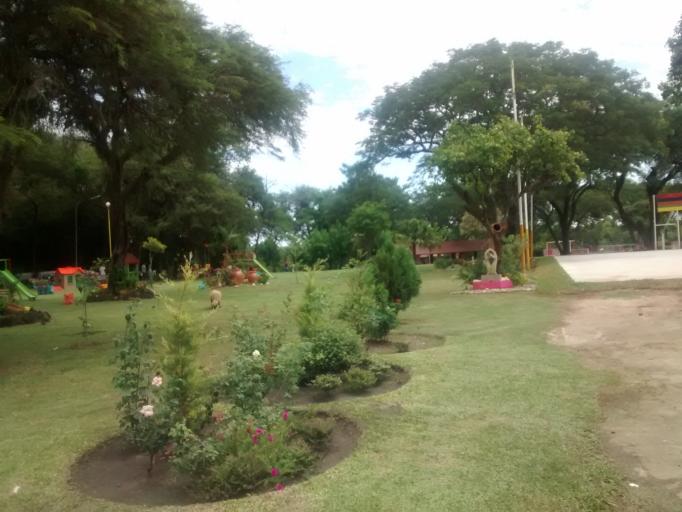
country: AR
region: Chaco
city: Fontana
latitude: -27.4025
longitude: -59.0153
